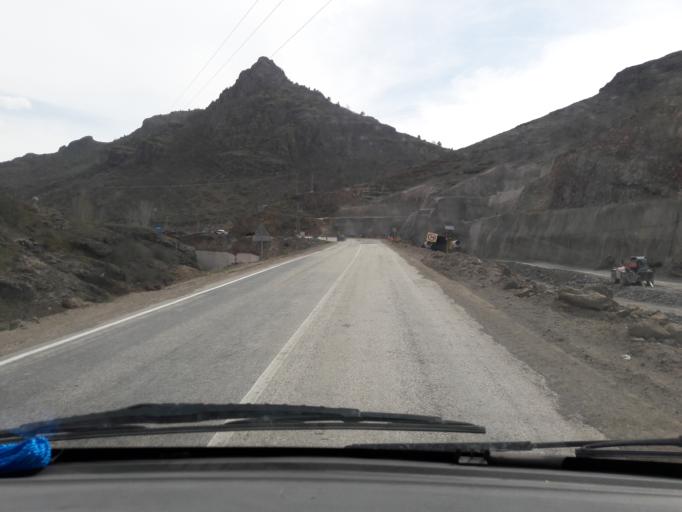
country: TR
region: Gumushane
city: Gumushkhane
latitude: 40.3010
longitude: 39.4737
